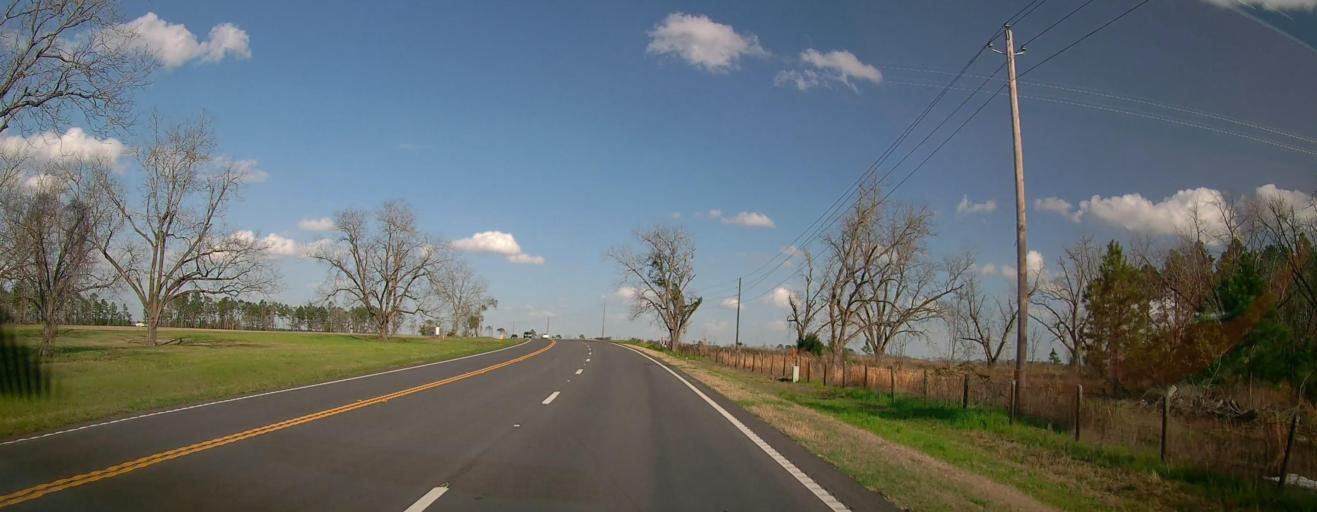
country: US
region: Georgia
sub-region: Montgomery County
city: Mount Vernon
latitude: 32.1799
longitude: -82.5535
